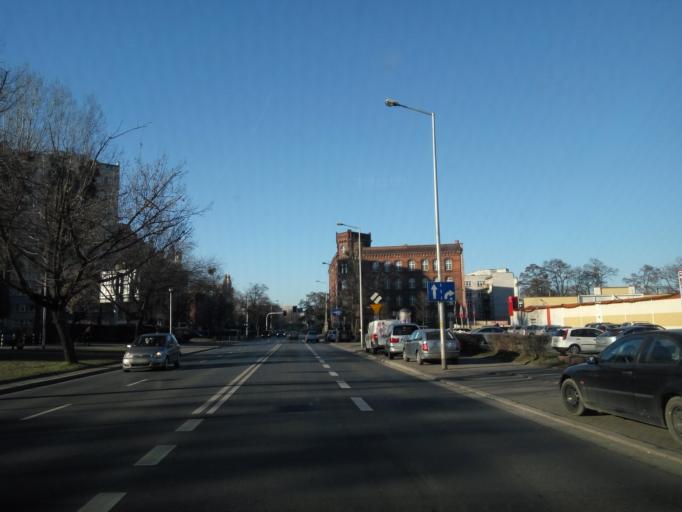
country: PL
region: Lower Silesian Voivodeship
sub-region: Powiat wroclawski
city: Wroclaw
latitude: 51.0999
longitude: 17.0248
